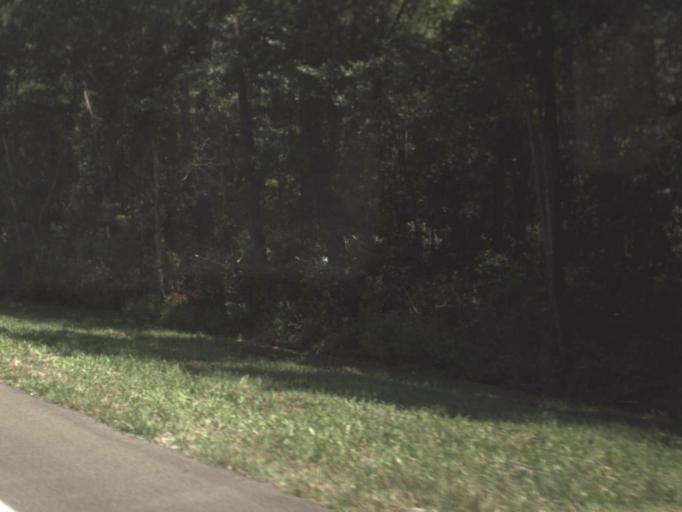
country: US
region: Florida
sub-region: Alachua County
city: Alachua
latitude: 29.7698
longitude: -82.3670
